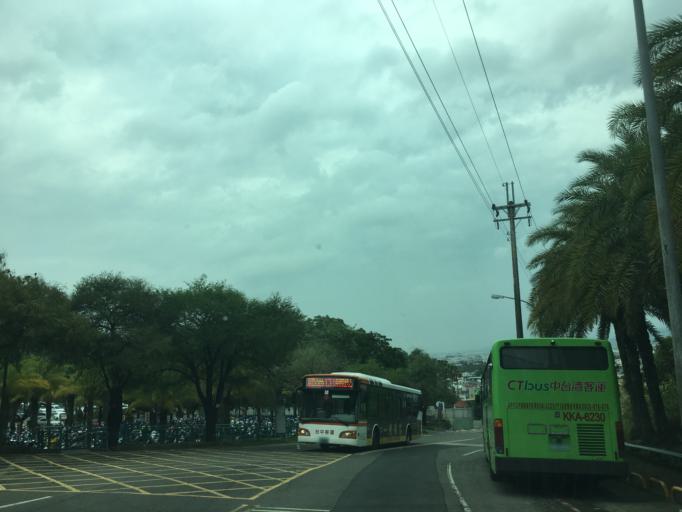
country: TW
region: Taiwan
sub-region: Taichung City
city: Taichung
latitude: 24.0694
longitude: 120.7156
